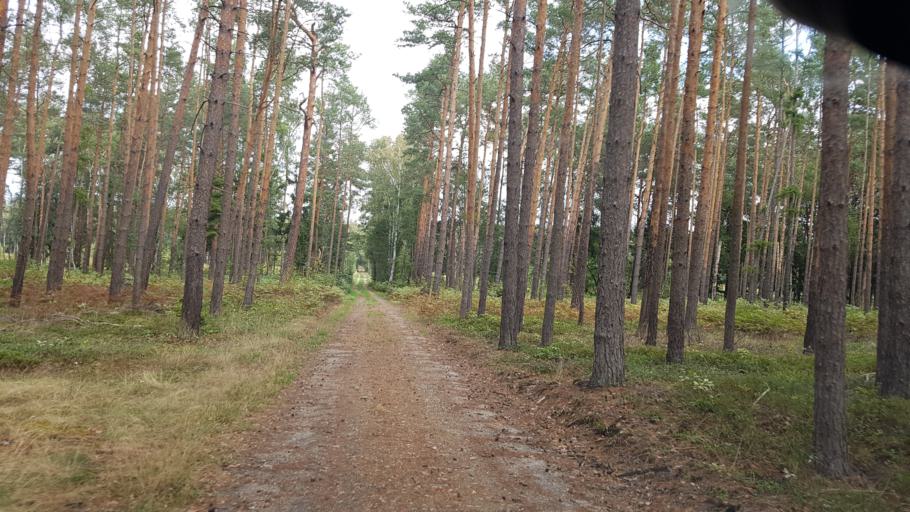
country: DE
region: Brandenburg
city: Ruckersdorf
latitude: 51.5522
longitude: 13.6360
